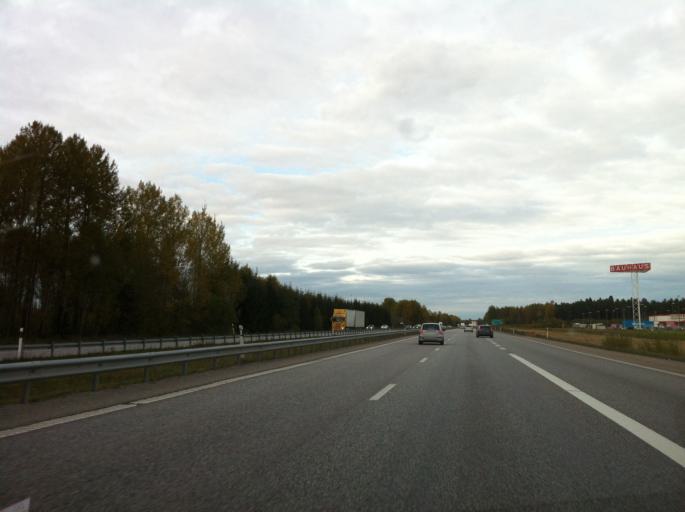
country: SE
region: OErebro
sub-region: Kumla Kommun
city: Kumla
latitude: 59.2106
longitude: 15.1302
